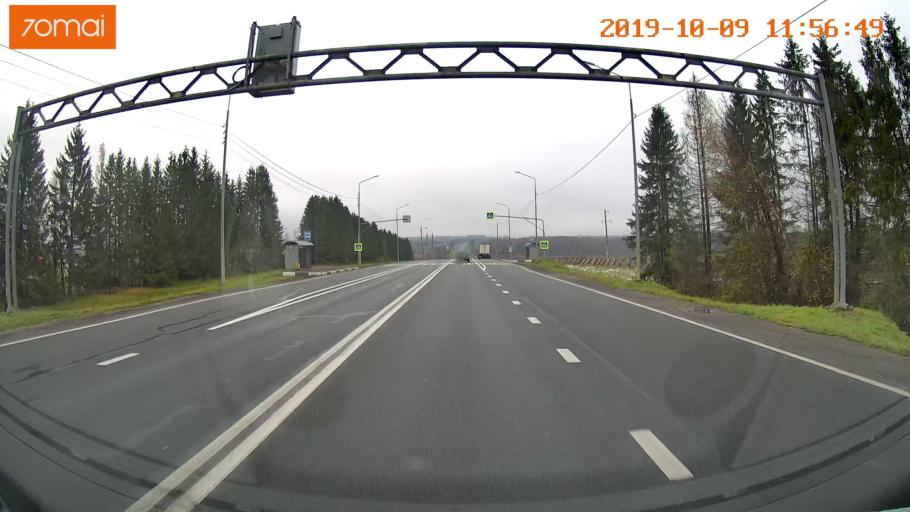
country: RU
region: Vologda
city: Gryazovets
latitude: 58.7400
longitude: 40.2893
